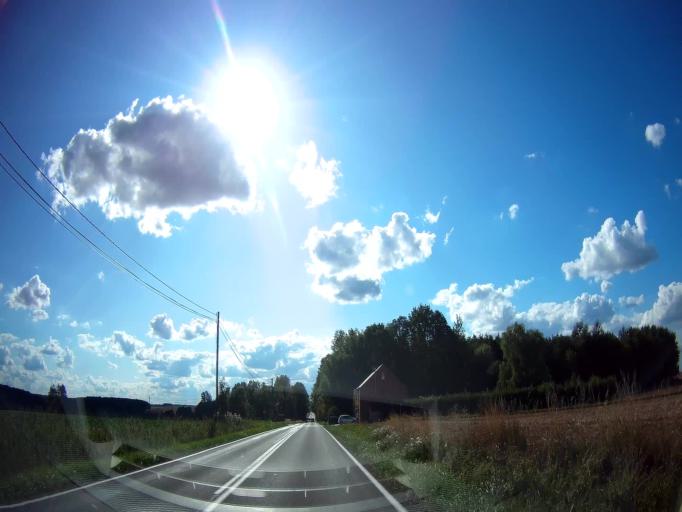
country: BE
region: Wallonia
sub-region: Province de Namur
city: Mettet
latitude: 50.3165
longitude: 4.7143
